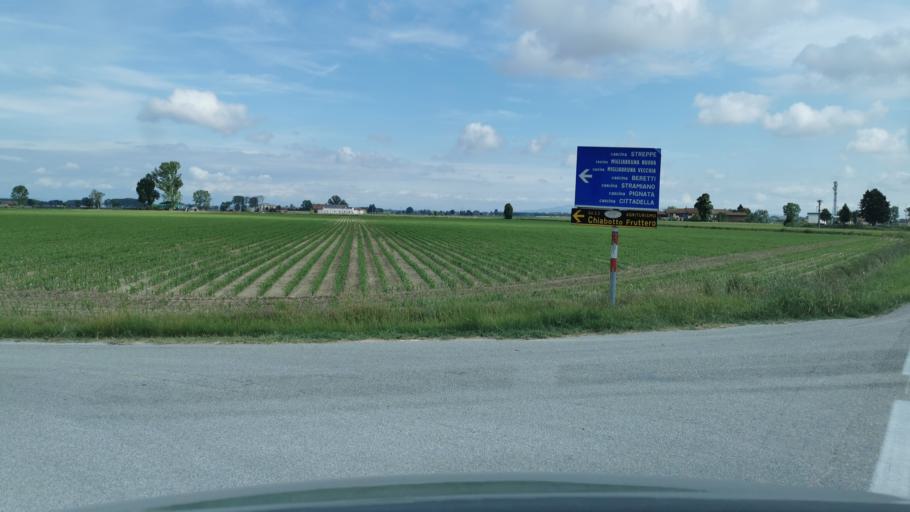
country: IT
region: Piedmont
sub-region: Provincia di Torino
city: Carmagnola
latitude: 44.8100
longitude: 7.6976
